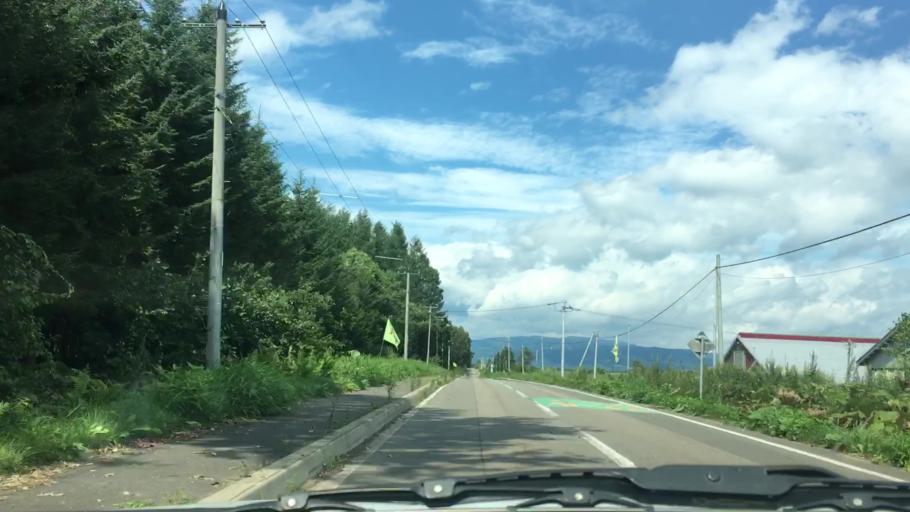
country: JP
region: Hokkaido
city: Otofuke
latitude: 43.2685
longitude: 143.3863
